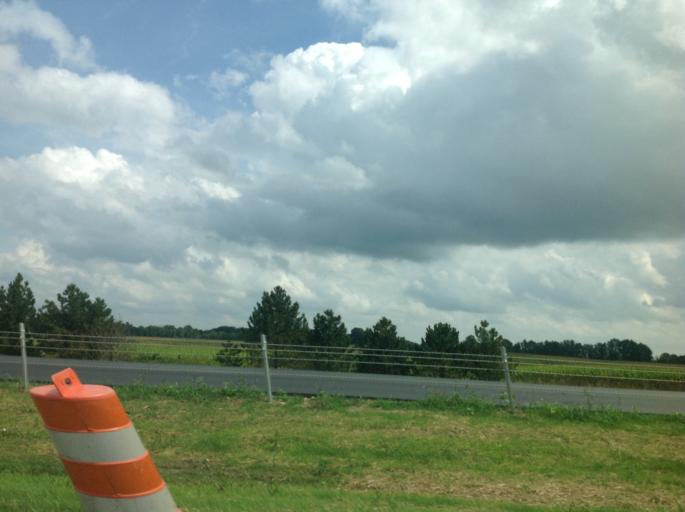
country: US
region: Ohio
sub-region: Delaware County
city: Sunbury
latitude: 40.3155
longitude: -82.9118
